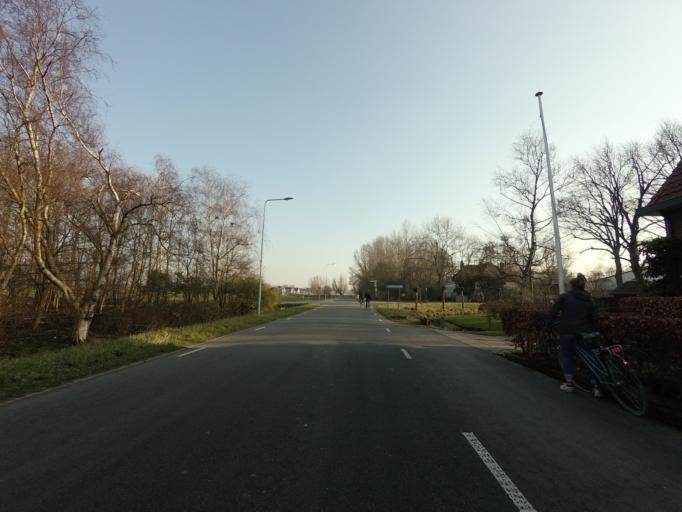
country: NL
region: North Holland
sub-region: Gemeente Haarlem
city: Haarlem
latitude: 52.3924
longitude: 4.6790
